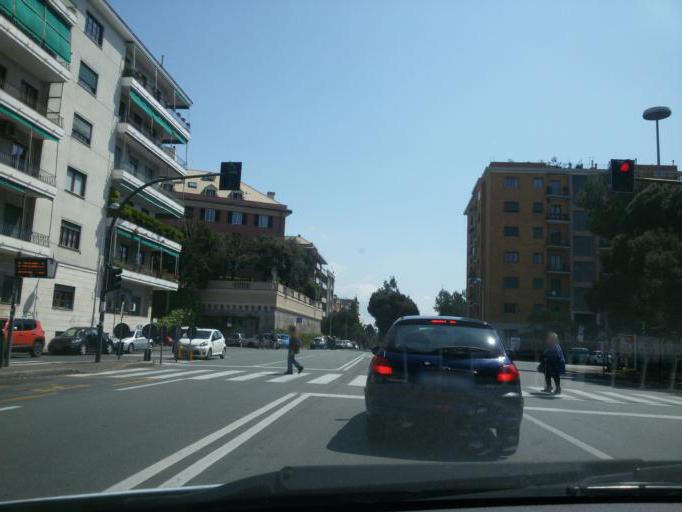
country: IT
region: Liguria
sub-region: Provincia di Genova
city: Genoa
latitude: 44.3979
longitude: 8.9646
